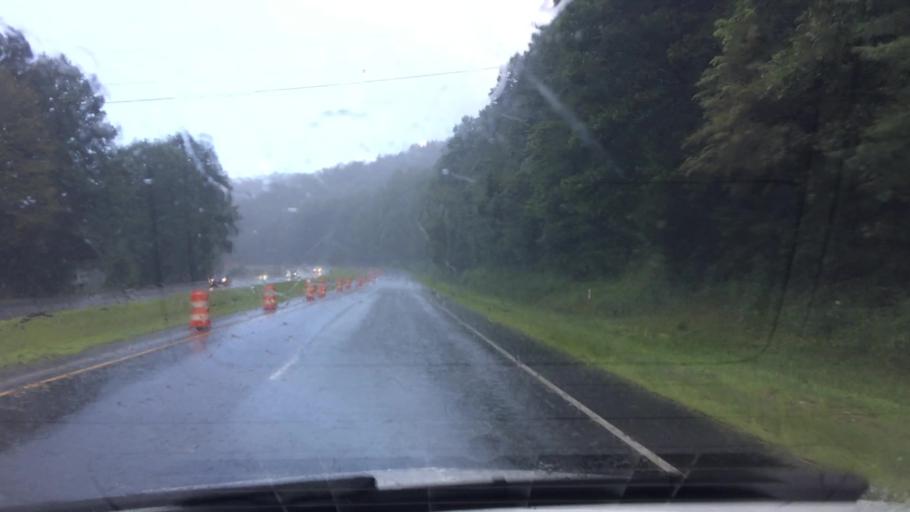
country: US
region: North Carolina
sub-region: Wilkes County
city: Millers Creek
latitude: 36.2011
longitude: -81.4325
